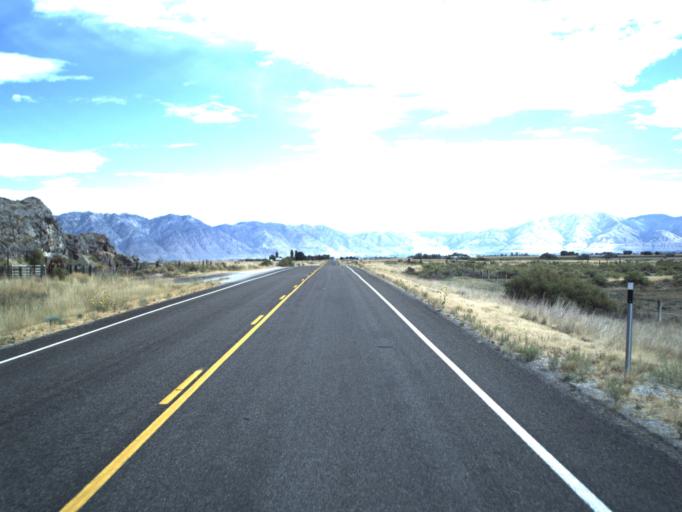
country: US
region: Utah
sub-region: Box Elder County
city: Elwood
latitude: 41.5770
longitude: -112.2357
